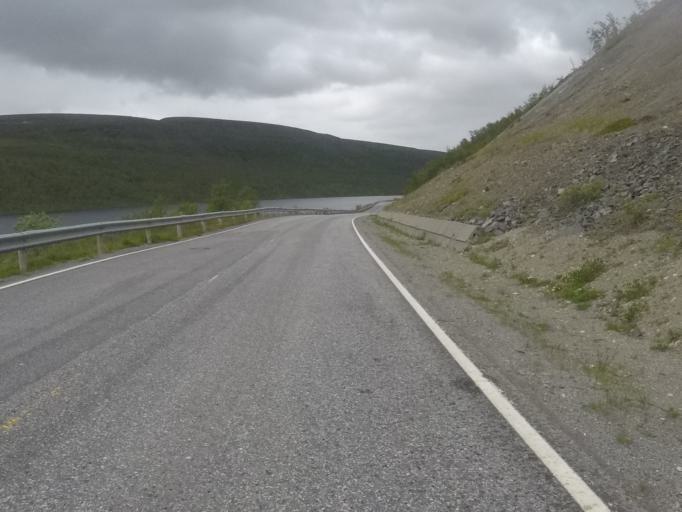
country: NO
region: Finnmark Fylke
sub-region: Alta
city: Alta
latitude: 69.7013
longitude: 23.4106
